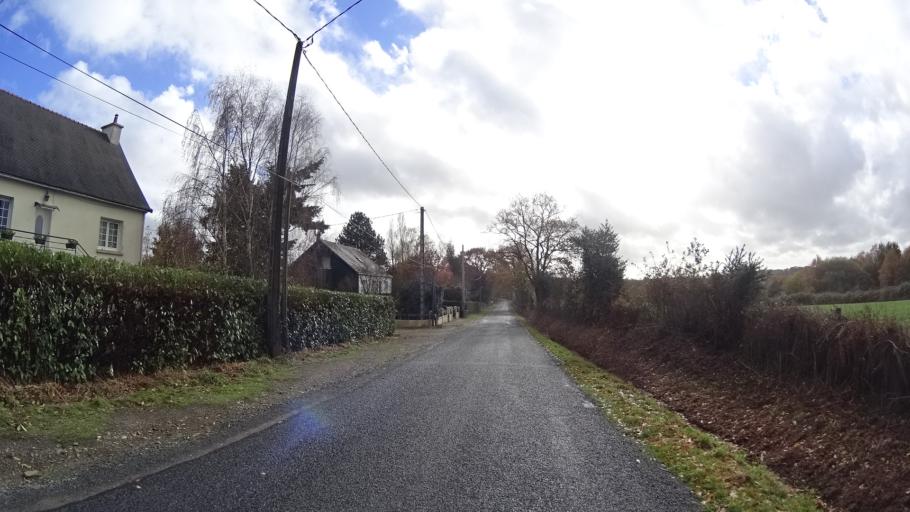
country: FR
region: Pays de la Loire
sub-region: Departement de la Loire-Atlantique
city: Fegreac
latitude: 47.6090
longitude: -2.0672
